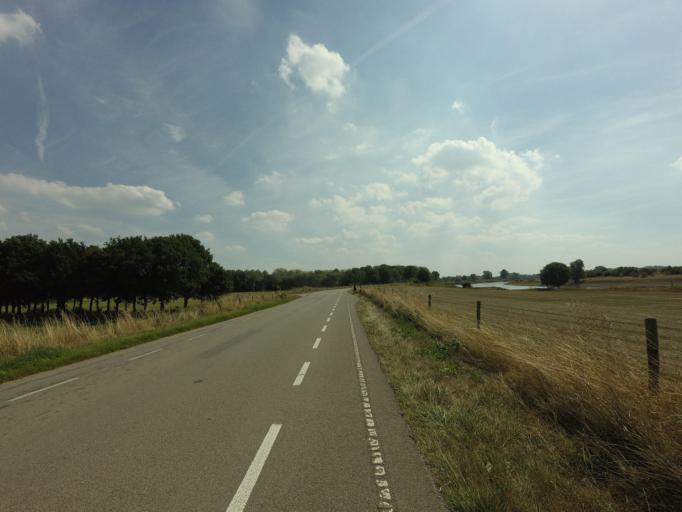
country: NL
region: Gelderland
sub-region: Gemeente Rheden
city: De Steeg
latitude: 52.0125
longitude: 6.0760
